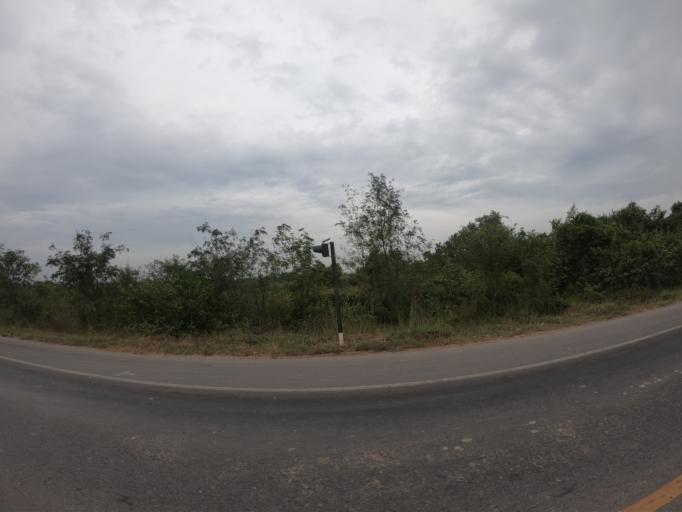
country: TH
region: Roi Et
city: Chiang Khwan
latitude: 16.1182
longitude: 103.8462
